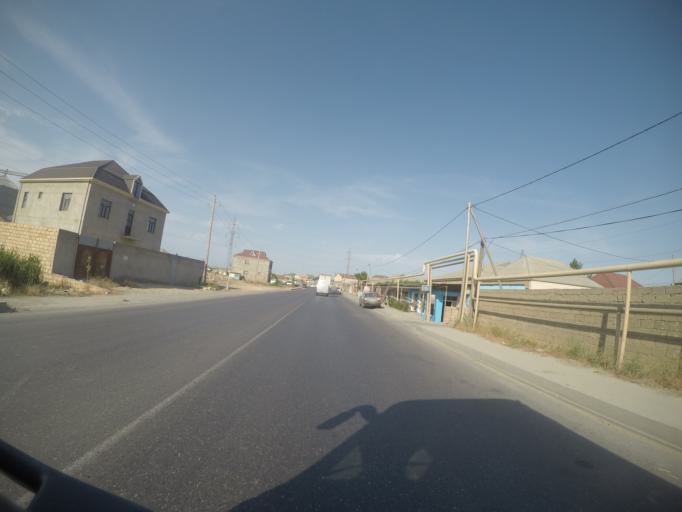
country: AZ
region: Baki
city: Bilajari
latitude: 40.4484
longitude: 49.8019
